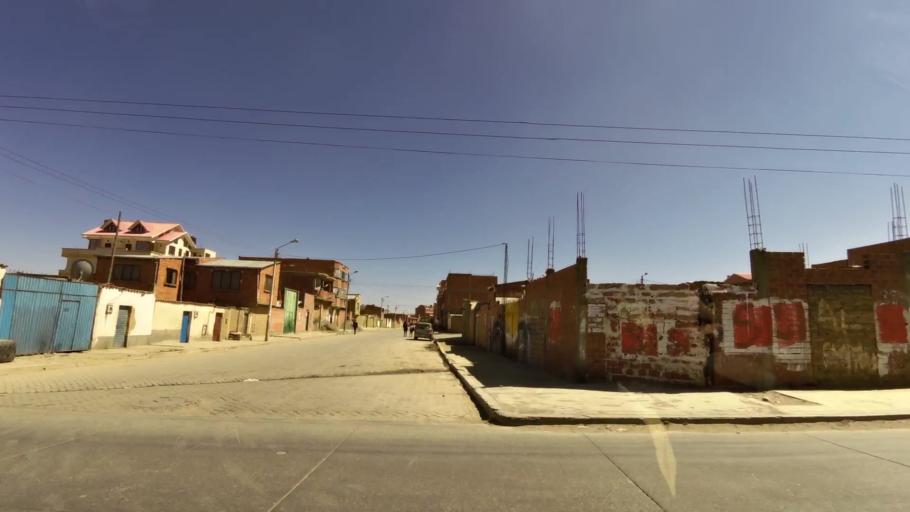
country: BO
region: La Paz
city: La Paz
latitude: -16.4979
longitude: -68.2072
